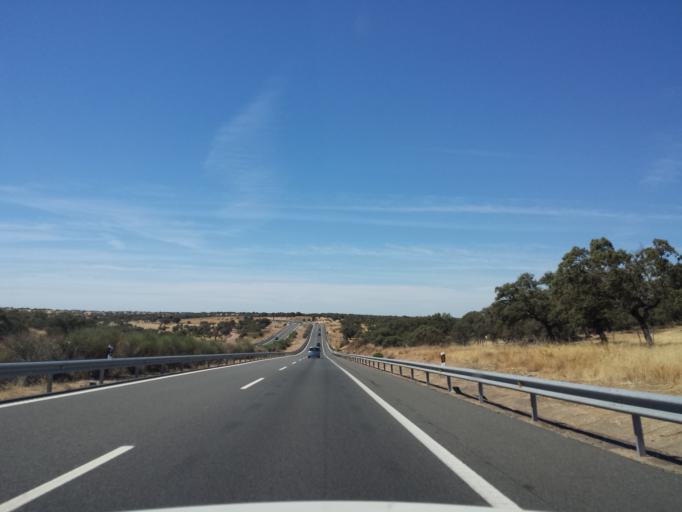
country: ES
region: Extremadura
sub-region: Provincia de Caceres
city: Jaraicejo
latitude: 39.6153
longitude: -5.8315
